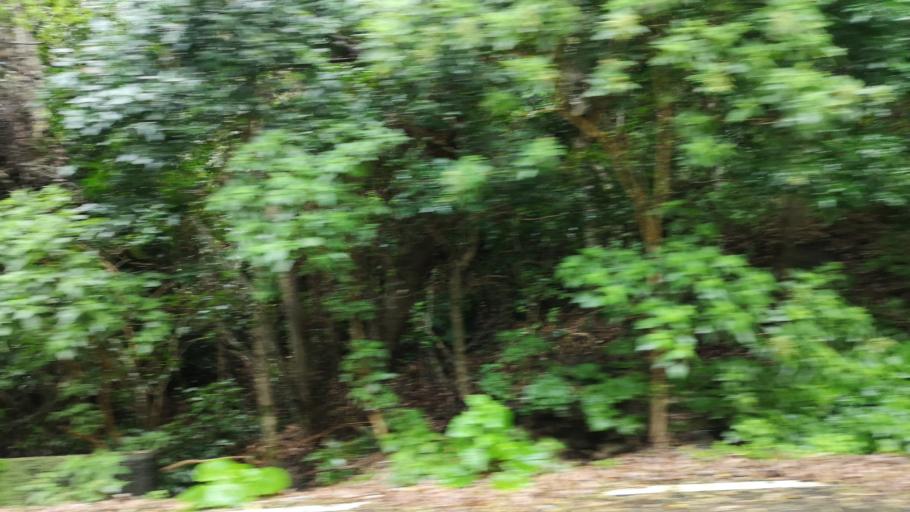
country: ES
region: Canary Islands
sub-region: Provincia de Santa Cruz de Tenerife
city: Hermigua
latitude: 28.1249
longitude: -17.2094
